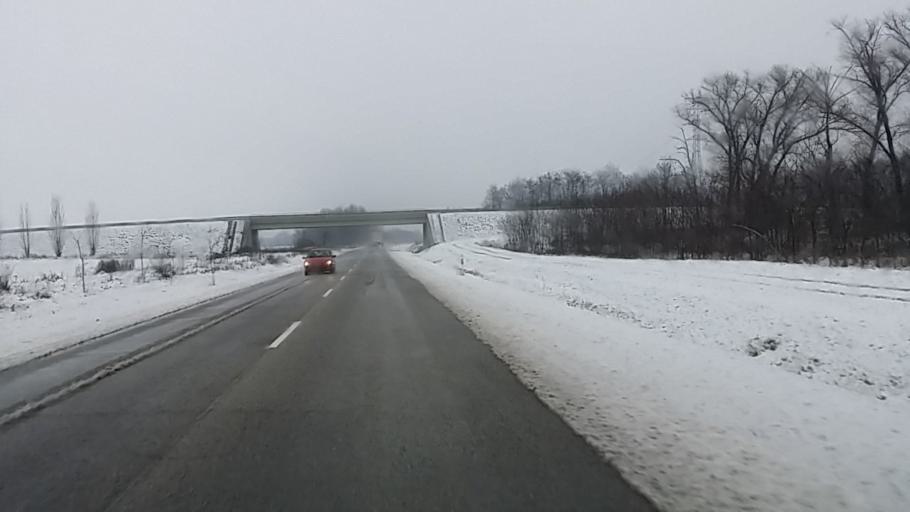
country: HU
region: Komarom-Esztergom
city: Komarom
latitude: 47.7291
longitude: 18.1024
